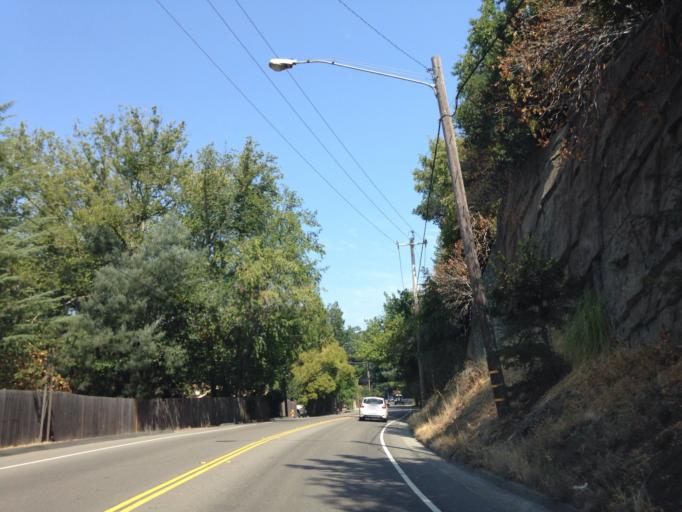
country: US
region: California
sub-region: Marin County
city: Ross
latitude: 37.9655
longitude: -122.5581
